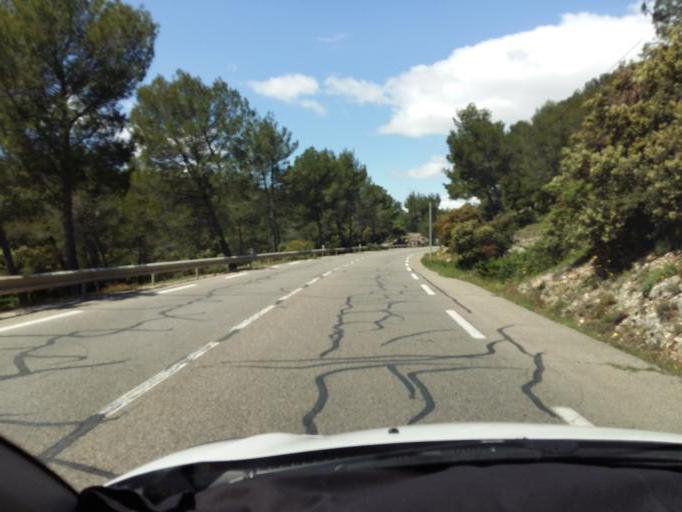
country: FR
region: Provence-Alpes-Cote d'Azur
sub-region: Departement des Bouches-du-Rhone
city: Lambesc
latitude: 43.6475
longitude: 5.2749
